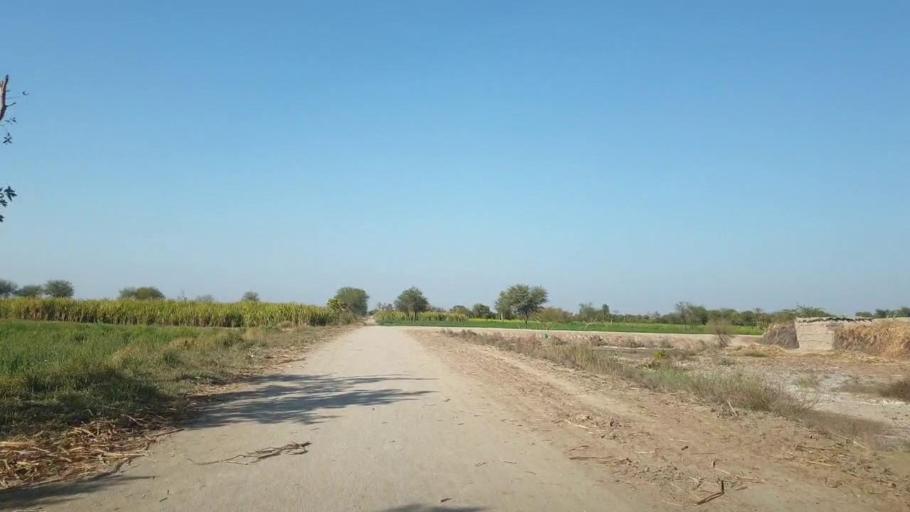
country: PK
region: Sindh
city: Mirpur Khas
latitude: 25.6296
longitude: 69.0694
